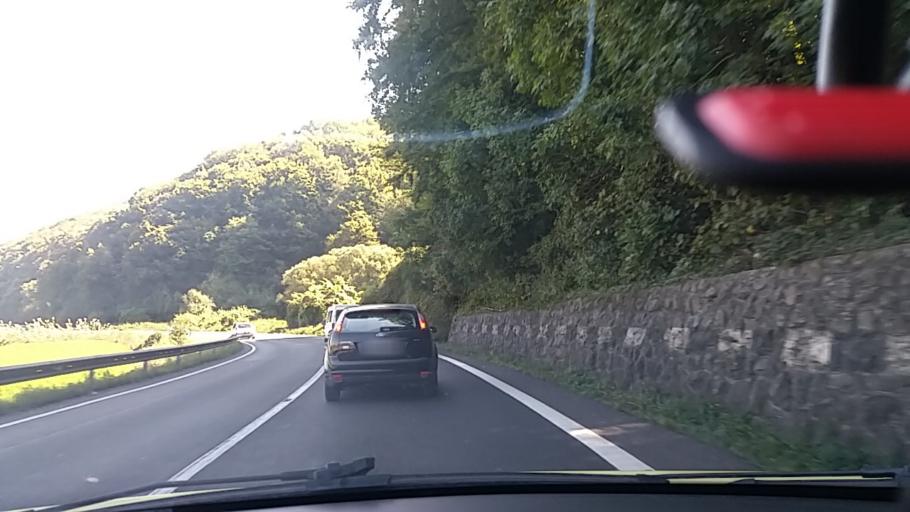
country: RO
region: Hunedoara
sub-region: Comuna Ilia
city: Ilia
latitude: 45.9207
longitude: 22.7024
